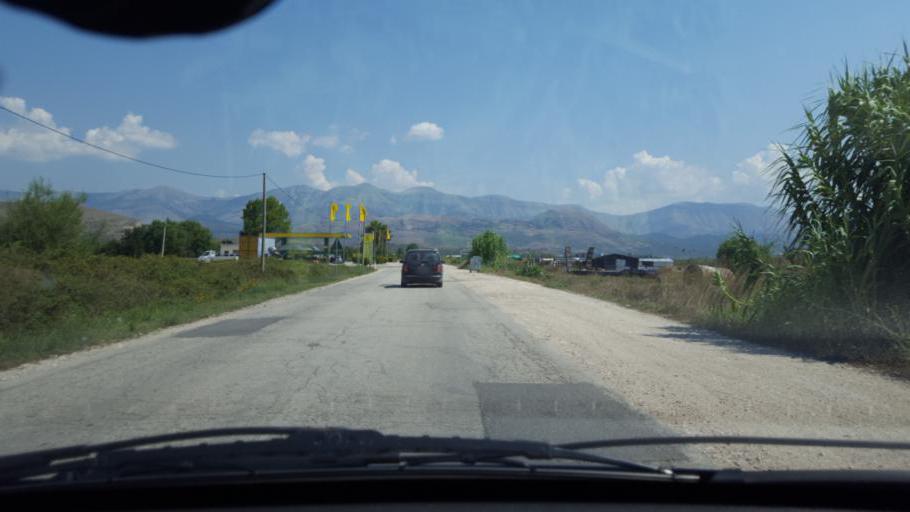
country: AL
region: Vlore
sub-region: Rrethi i Delvines
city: Finiq
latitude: 39.8844
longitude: 20.0569
